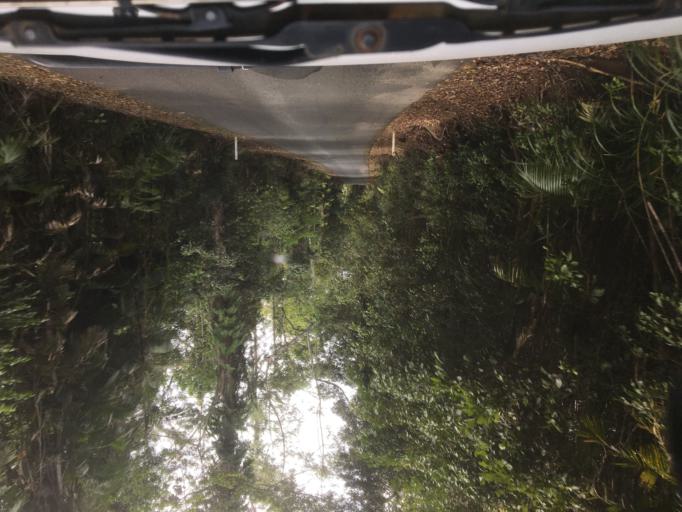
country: AU
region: Queensland
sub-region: Tablelands
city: Tolga
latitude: -17.2808
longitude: 145.6207
